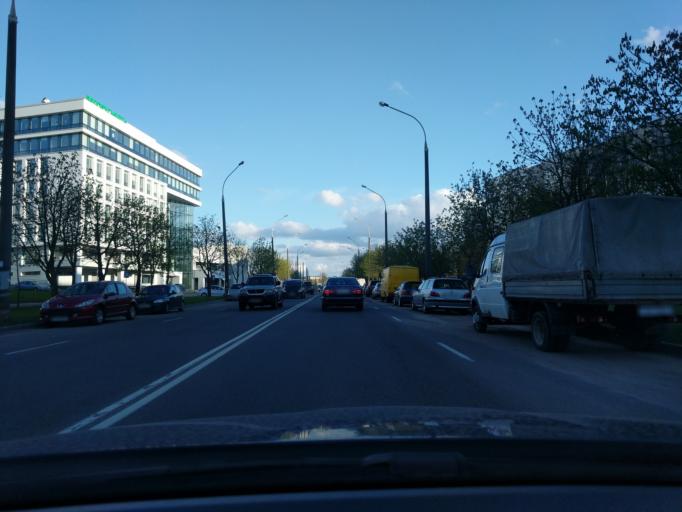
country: BY
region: Minsk
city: Novoye Medvezhino
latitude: 53.9101
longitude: 27.4521
